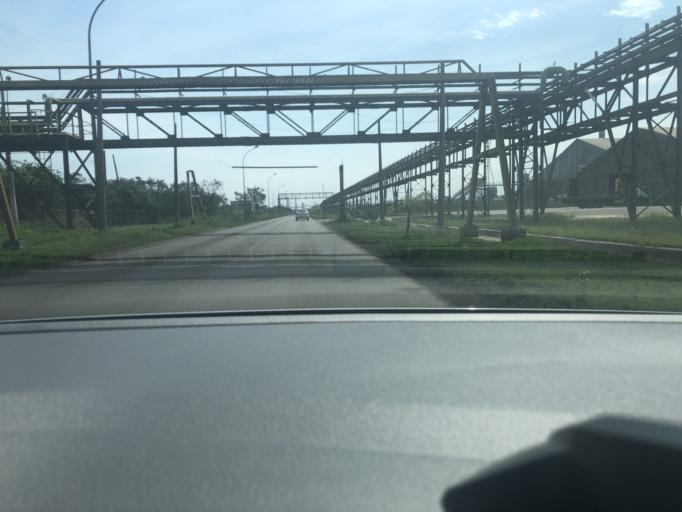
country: BR
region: Rio de Janeiro
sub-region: Itaguai
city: Itaguai
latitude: -22.9138
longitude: -43.7370
